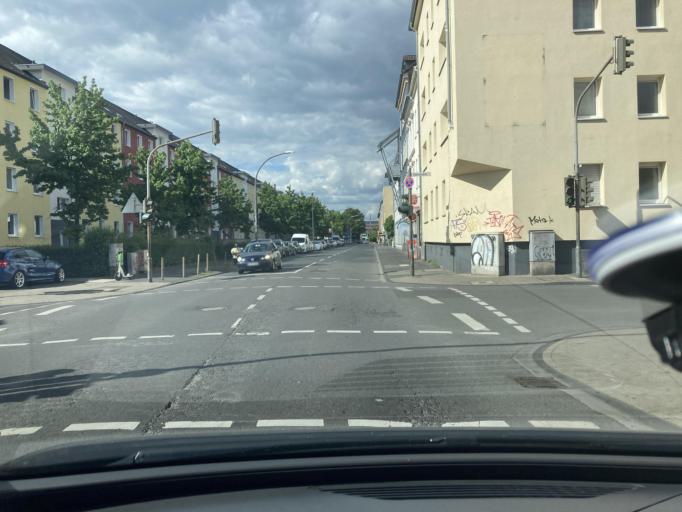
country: DE
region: North Rhine-Westphalia
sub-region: Regierungsbezirk Koln
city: Humboldtkolonie
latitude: 50.9303
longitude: 7.0002
